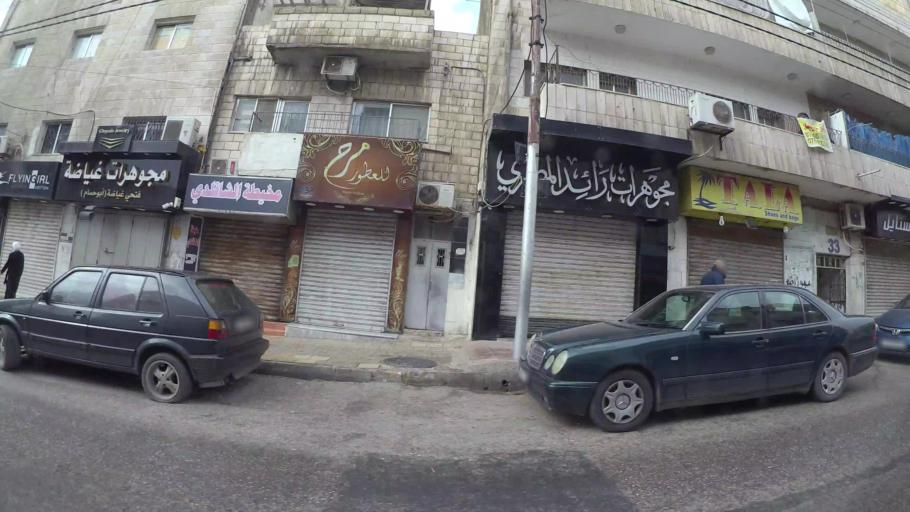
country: JO
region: Amman
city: Amman
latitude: 31.9743
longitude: 35.9261
